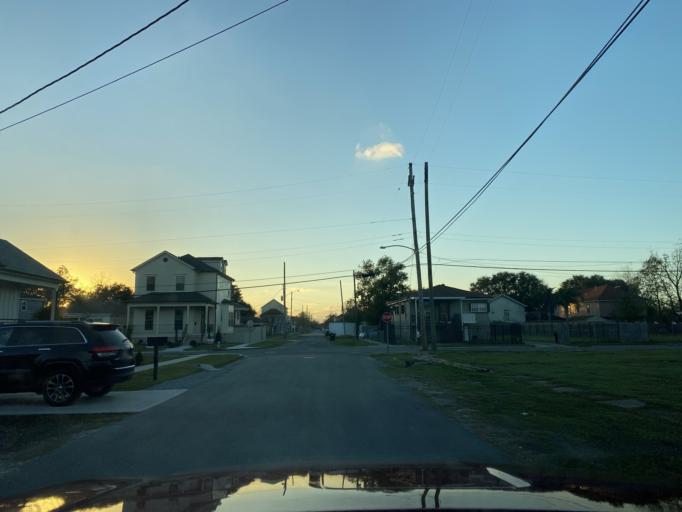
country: US
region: Louisiana
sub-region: Orleans Parish
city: New Orleans
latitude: 30.0203
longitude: -90.0547
